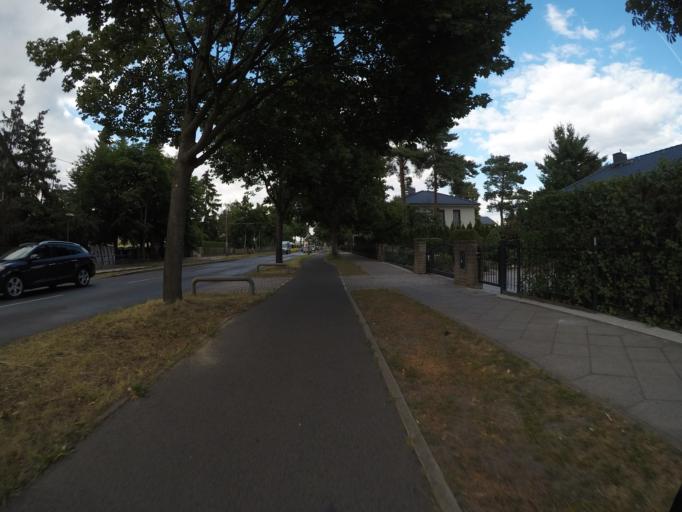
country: DE
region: Berlin
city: Mahlsdorf
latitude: 52.4840
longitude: 13.6027
